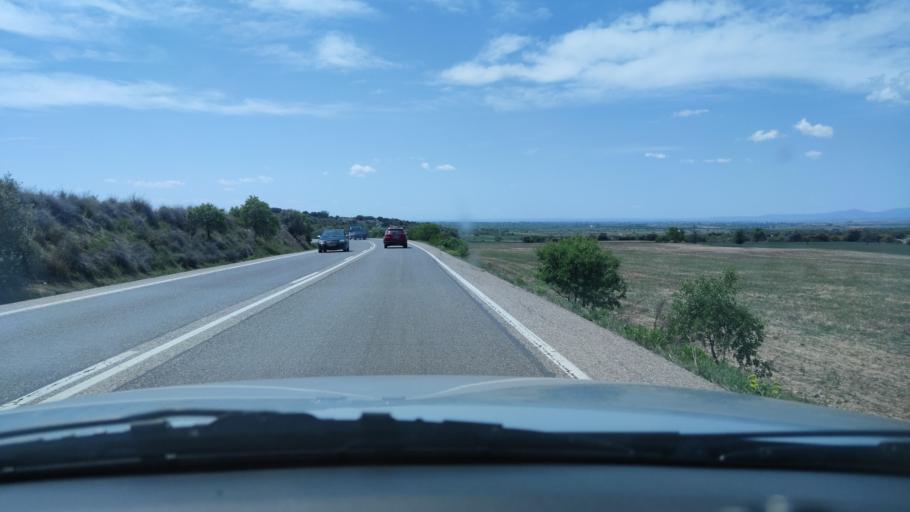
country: ES
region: Catalonia
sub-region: Provincia de Lleida
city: Tarrega
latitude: 41.6746
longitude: 1.1538
